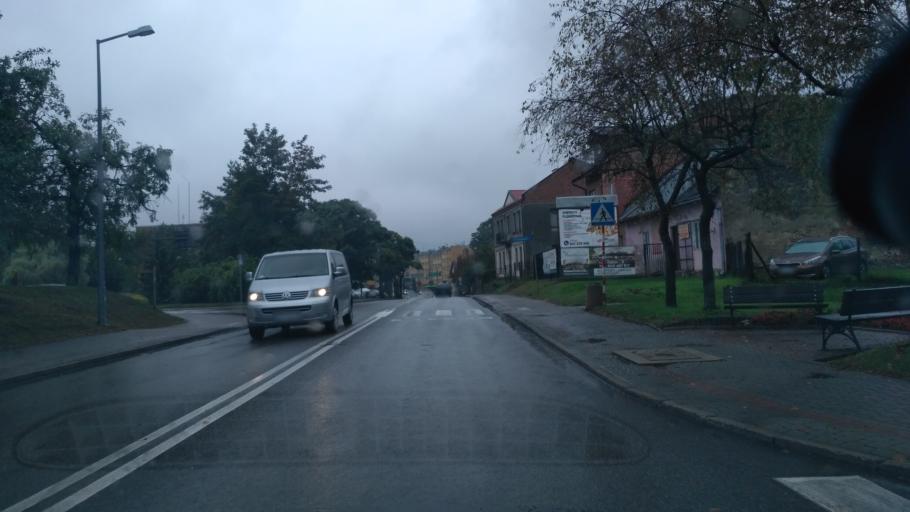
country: PL
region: Subcarpathian Voivodeship
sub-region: Powiat debicki
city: Debica
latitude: 50.0535
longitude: 21.4106
